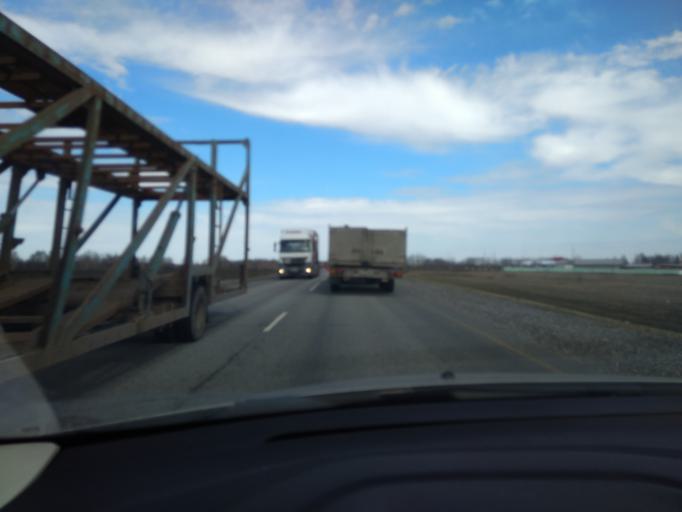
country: RU
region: Sverdlovsk
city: Pyshma
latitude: 56.9812
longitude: 63.2461
